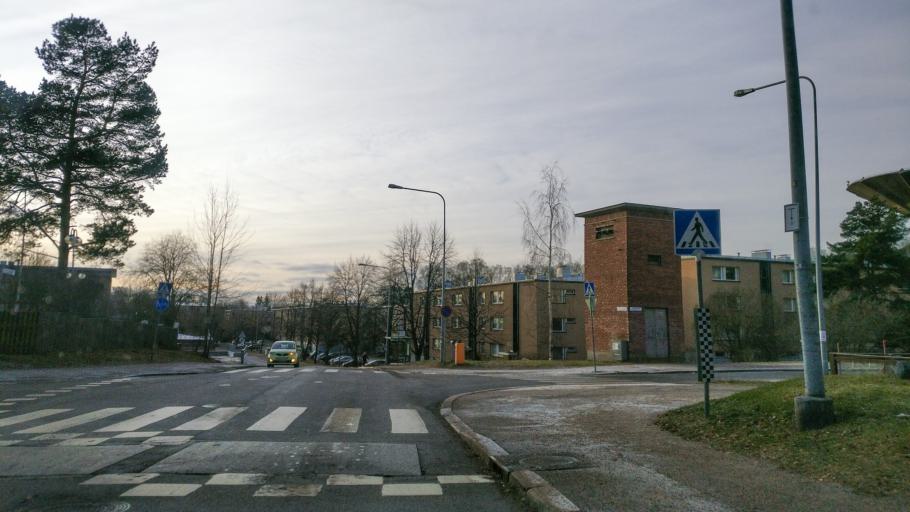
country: FI
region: Uusimaa
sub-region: Helsinki
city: Vantaa
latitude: 60.1979
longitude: 25.0556
